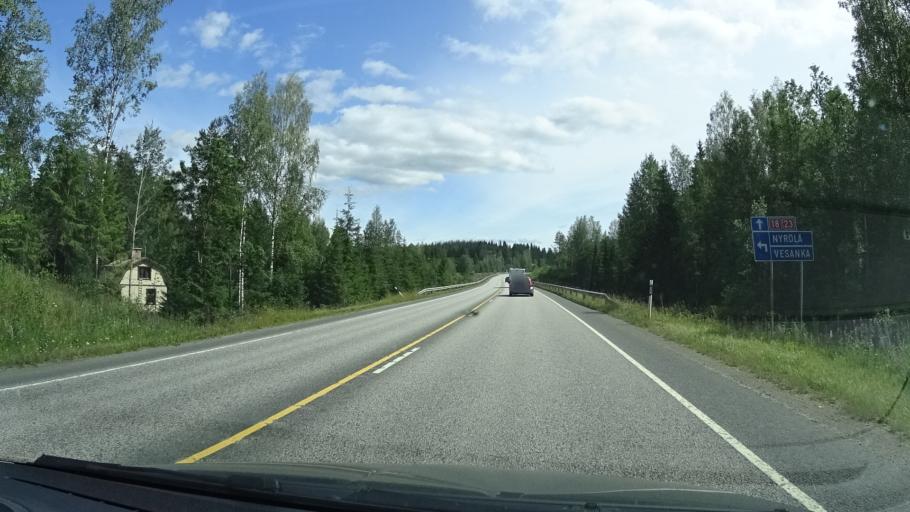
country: FI
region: Central Finland
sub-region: Jyvaeskylae
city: Jyvaeskylae
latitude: 62.2649
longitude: 25.5710
